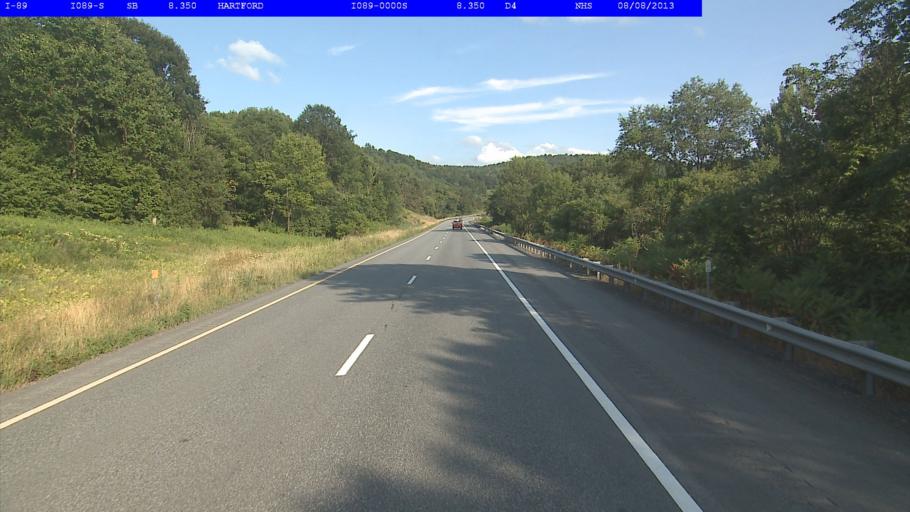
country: US
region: Vermont
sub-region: Windsor County
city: Wilder
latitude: 43.7229
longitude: -72.4195
